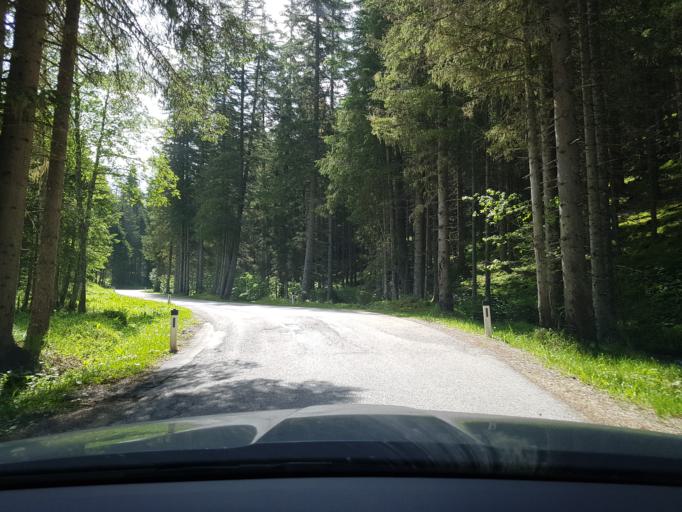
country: AT
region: Salzburg
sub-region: Politischer Bezirk Tamsweg
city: Thomatal
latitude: 47.0364
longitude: 13.7234
